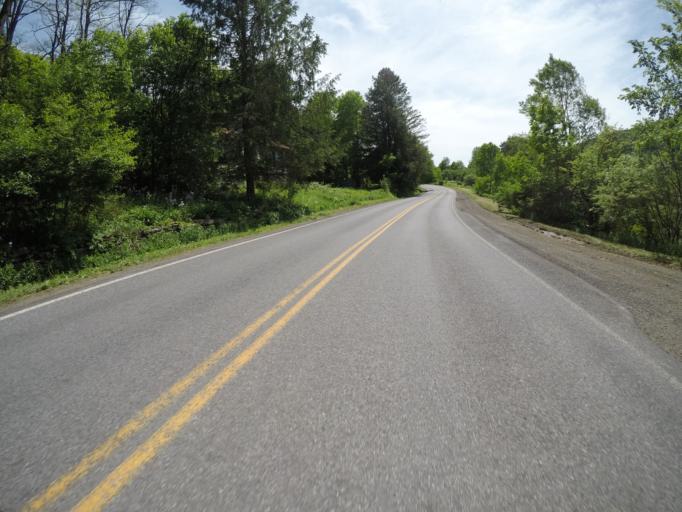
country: US
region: New York
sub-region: Delaware County
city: Delhi
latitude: 42.1383
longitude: -74.7999
